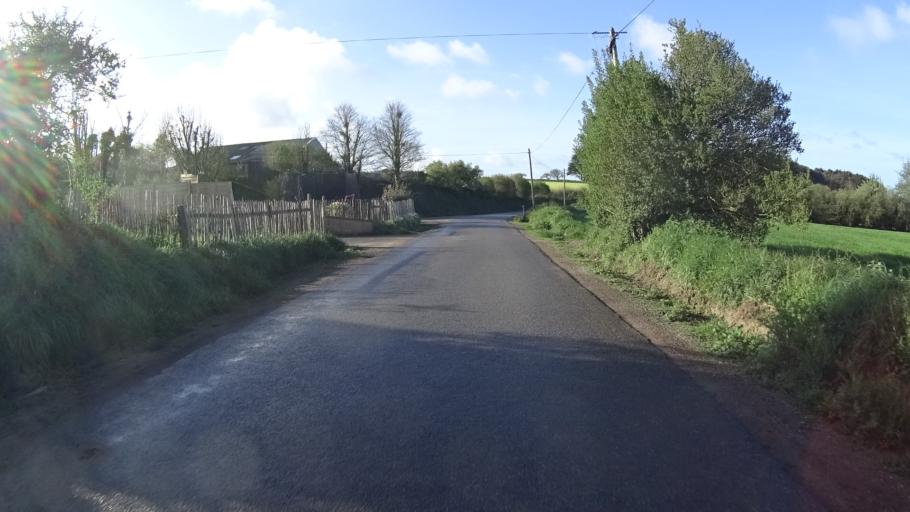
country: FR
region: Brittany
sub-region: Departement du Finistere
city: Plouarzel
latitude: 48.4272
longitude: -4.7042
